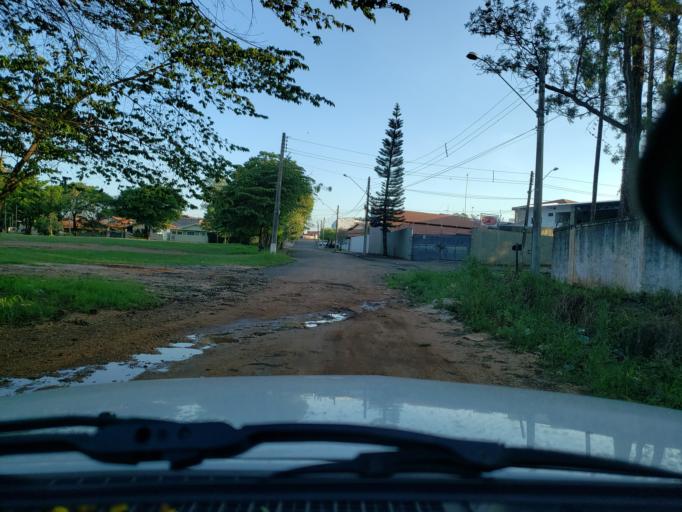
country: BR
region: Sao Paulo
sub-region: Moji-Guacu
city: Mogi-Gaucu
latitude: -22.3398
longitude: -46.9389
